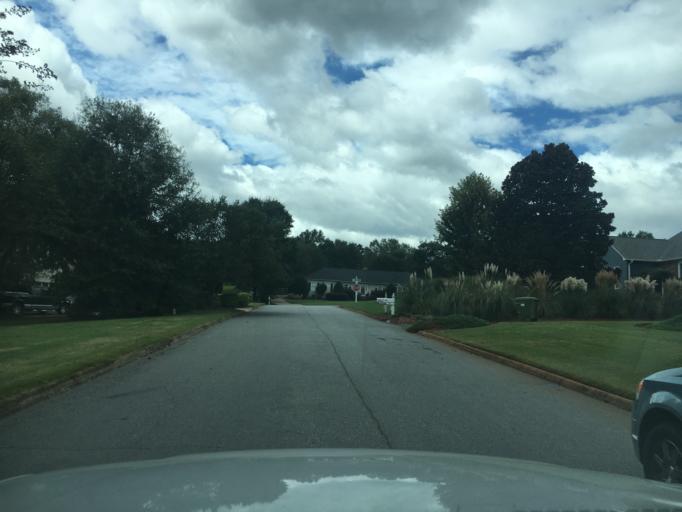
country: US
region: South Carolina
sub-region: Spartanburg County
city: Fairforest
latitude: 34.9020
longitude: -82.0511
